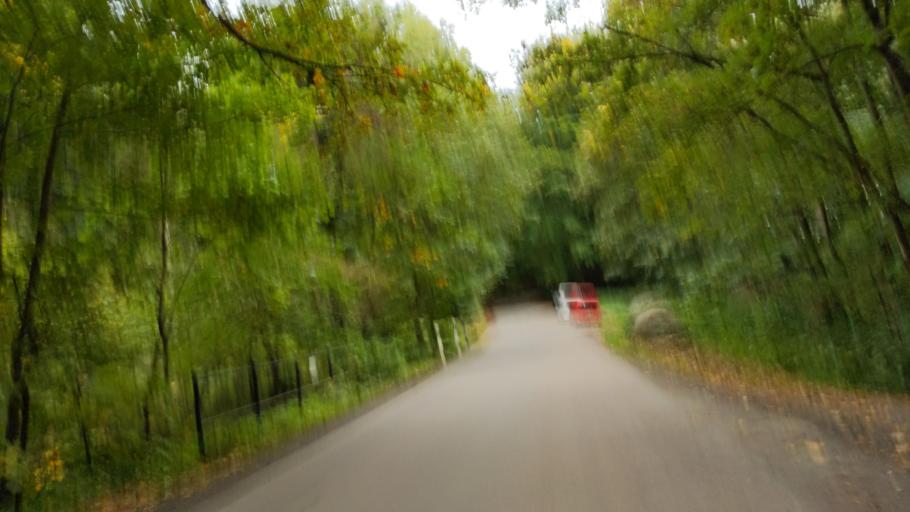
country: DE
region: Schleswig-Holstein
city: Neustadt in Holstein
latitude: 54.1357
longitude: 10.7855
